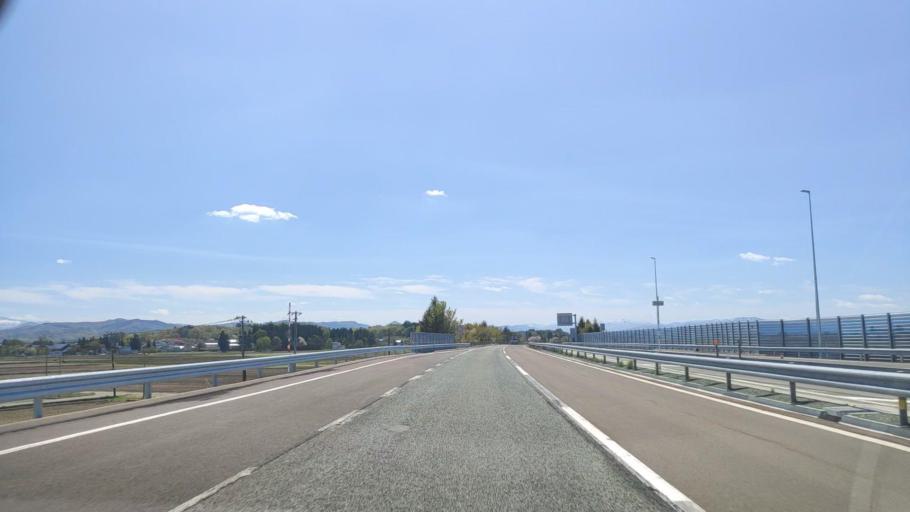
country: JP
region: Akita
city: Yokotemachi
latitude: 39.3243
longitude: 140.5136
